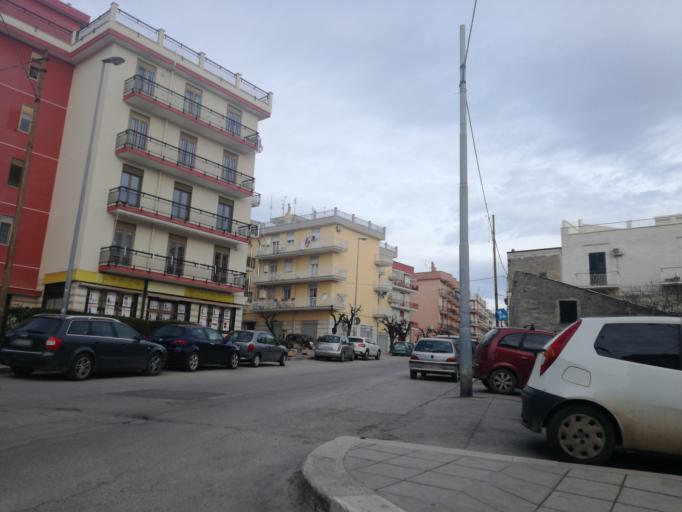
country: IT
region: Apulia
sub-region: Provincia di Bari
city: Ruvo di Puglia
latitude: 41.1188
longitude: 16.4784
